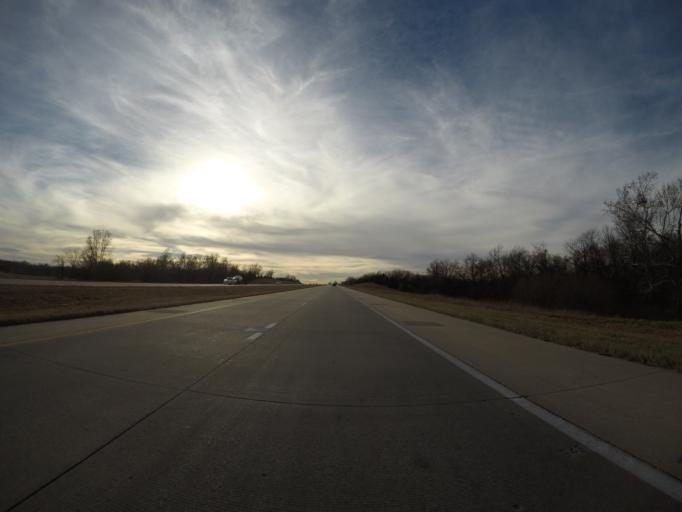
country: US
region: Kansas
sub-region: Franklin County
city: Ottawa
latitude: 38.5538
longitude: -95.3508
